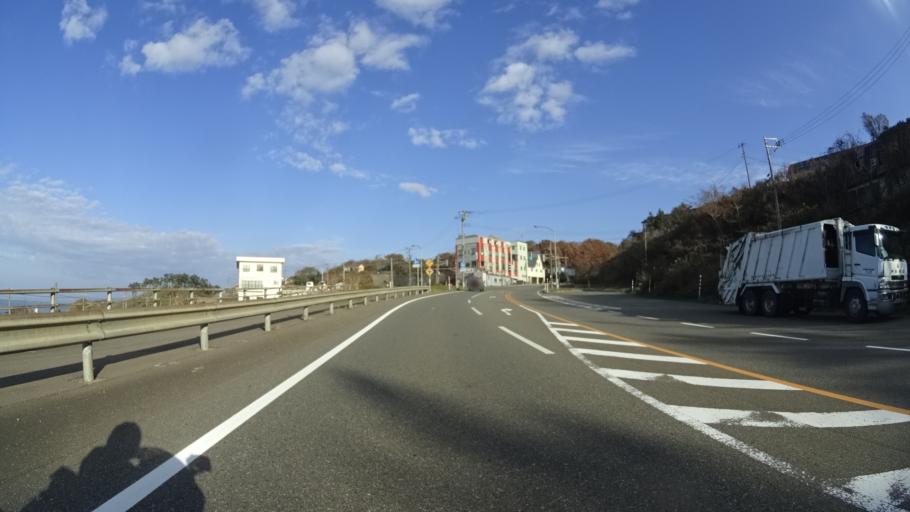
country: JP
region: Niigata
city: Kashiwazaki
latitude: 37.3528
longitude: 138.5063
